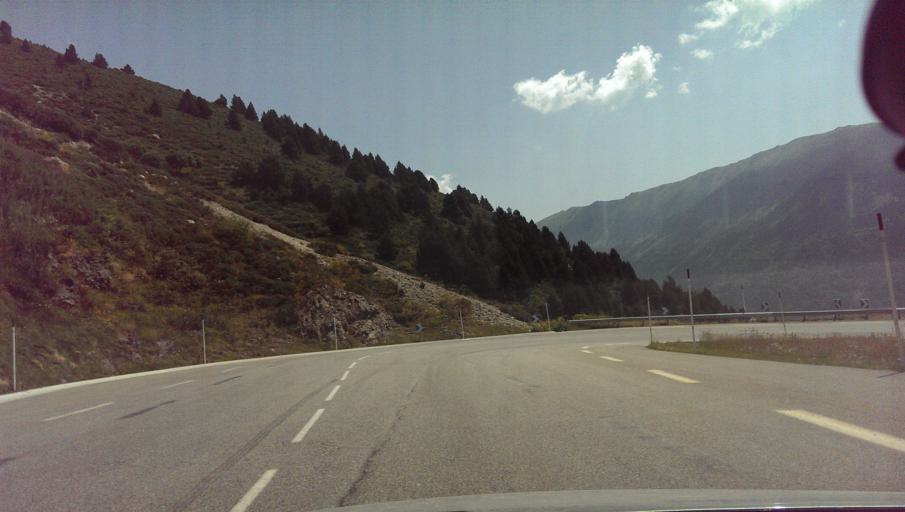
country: AD
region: Encamp
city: Pas de la Casa
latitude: 42.5539
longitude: 1.8237
